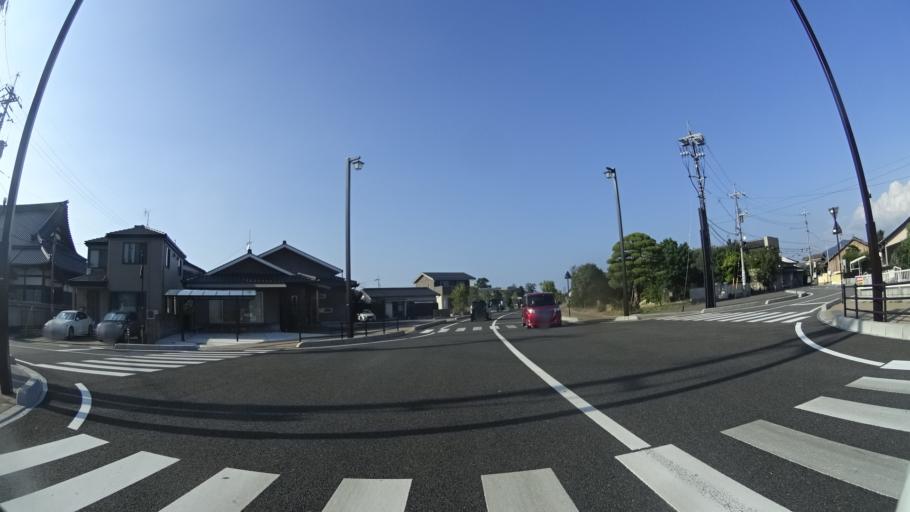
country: JP
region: Yamaguchi
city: Hagi
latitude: 34.4083
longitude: 131.3913
